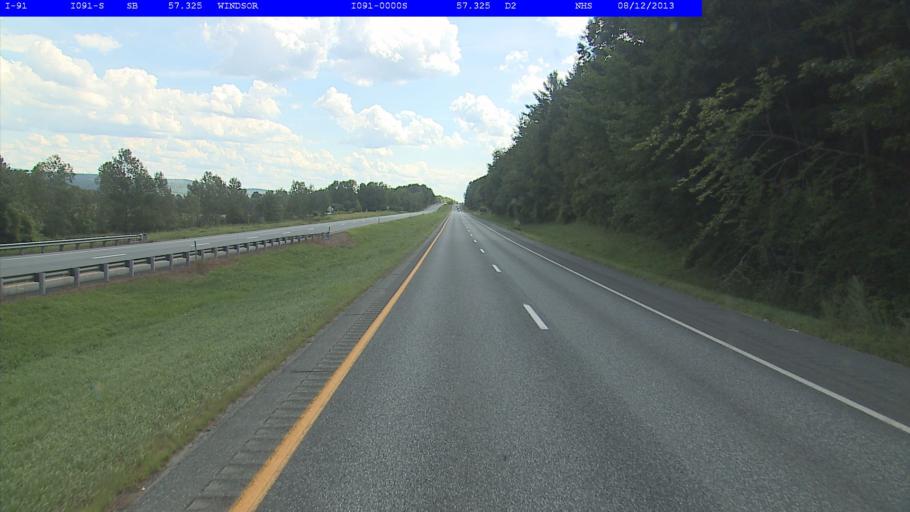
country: US
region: Vermont
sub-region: Windsor County
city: Windsor
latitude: 43.4853
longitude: -72.4072
